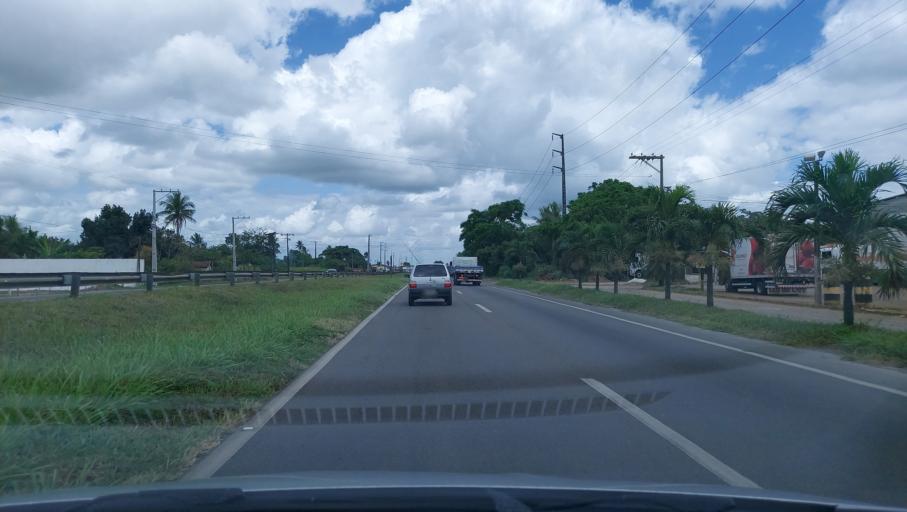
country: BR
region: Bahia
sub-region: Conceicao Do Jacuipe
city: Conceicao do Jacuipe
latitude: -12.3721
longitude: -38.8096
